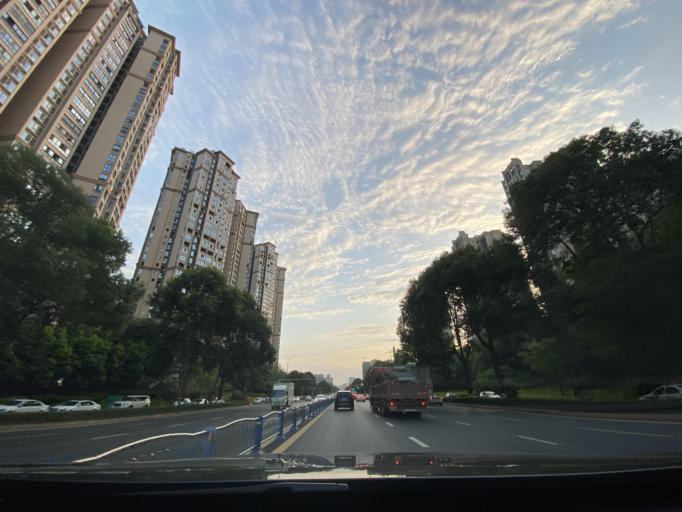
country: CN
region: Sichuan
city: Longquan
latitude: 30.5849
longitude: 104.2936
